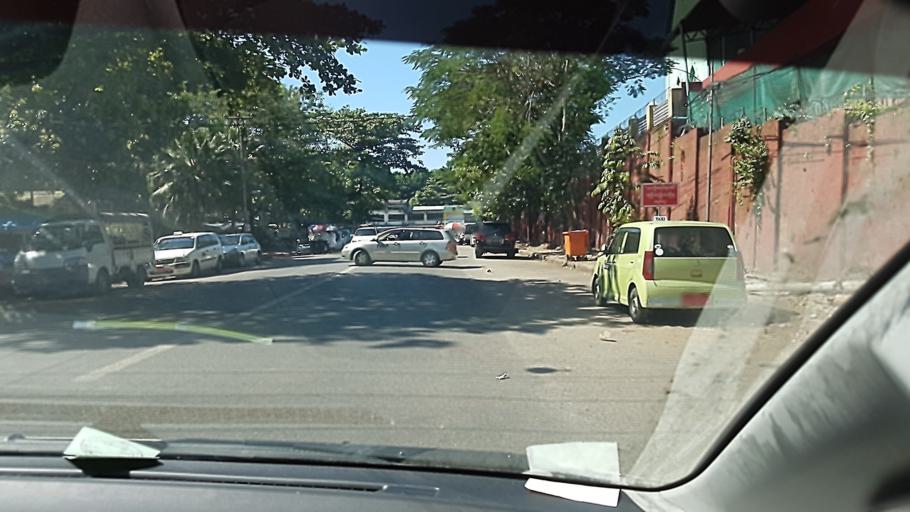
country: MM
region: Yangon
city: Yangon
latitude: 16.7836
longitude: 96.1635
